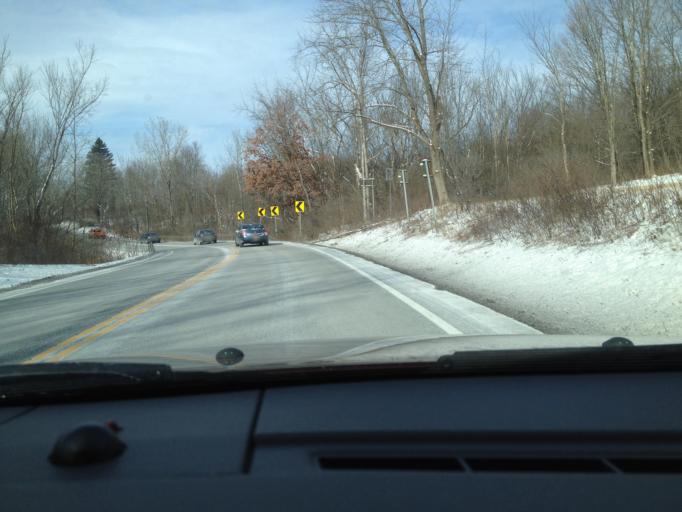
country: US
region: New York
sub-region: Rensselaer County
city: West Sand Lake
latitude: 42.6485
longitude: -73.6451
